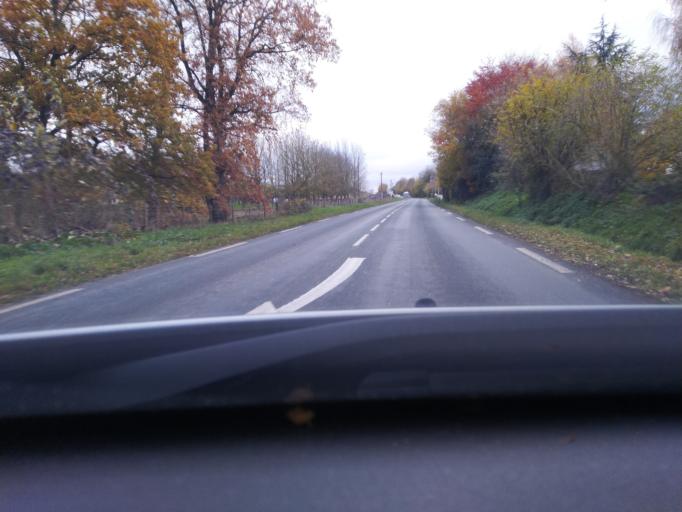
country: FR
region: Haute-Normandie
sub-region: Departement de la Seine-Maritime
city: La Vaupaliere
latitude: 49.4968
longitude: 0.9863
